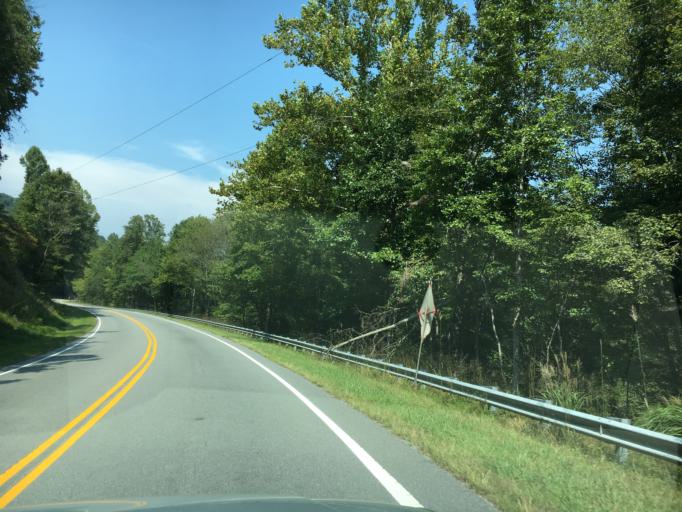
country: US
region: North Carolina
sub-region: McDowell County
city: West Marion
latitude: 35.5610
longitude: -81.9674
